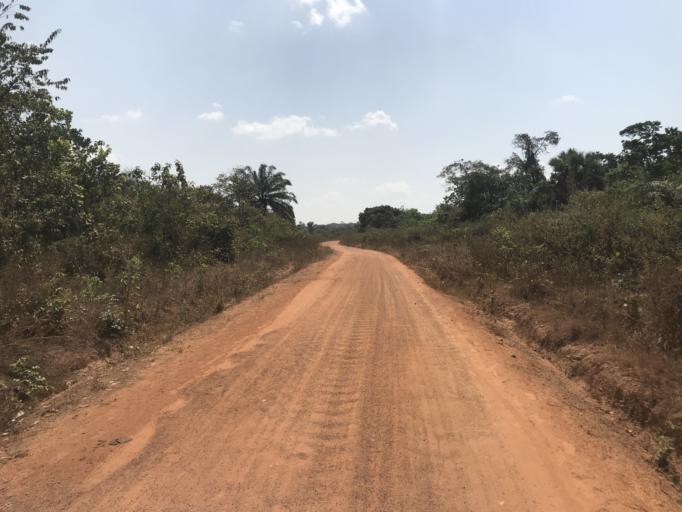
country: NG
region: Osun
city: Ifon
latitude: 7.9025
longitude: 4.4786
